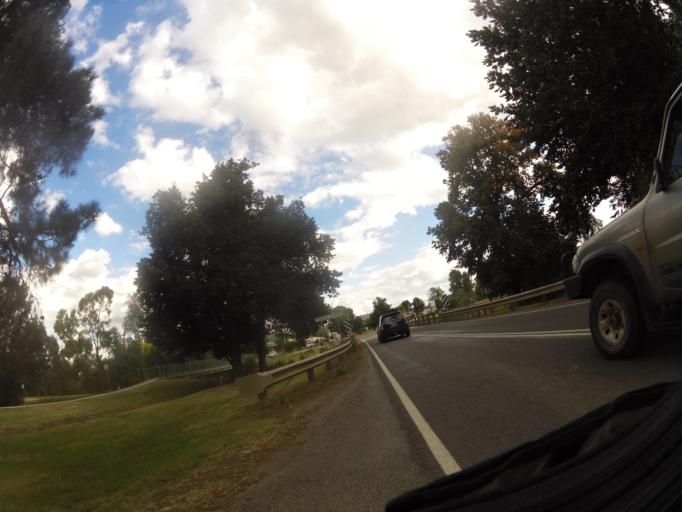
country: AU
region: Victoria
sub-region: Mansfield
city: Mansfield
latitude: -37.0490
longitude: 146.0888
